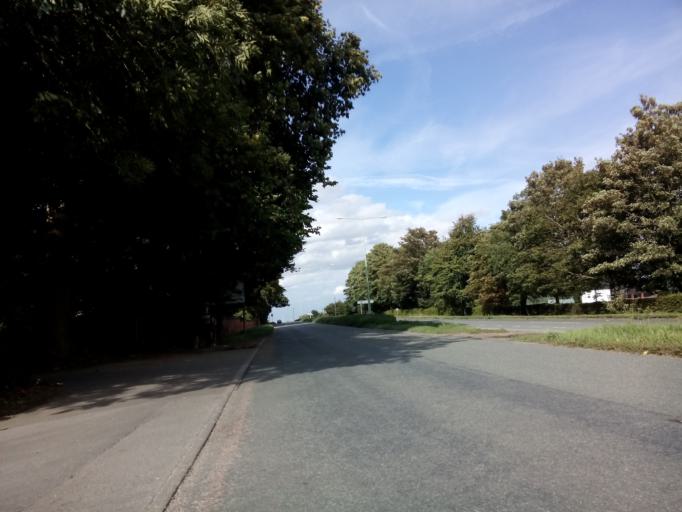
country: GB
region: England
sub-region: Suffolk
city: Capel Saint Mary
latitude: 52.0286
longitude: 1.0805
